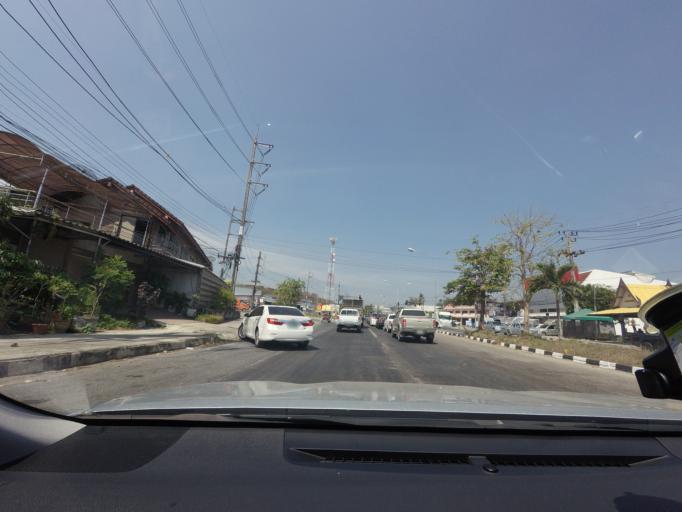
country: TH
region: Surat Thani
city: Kanchanadit
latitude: 9.1623
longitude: 99.4804
